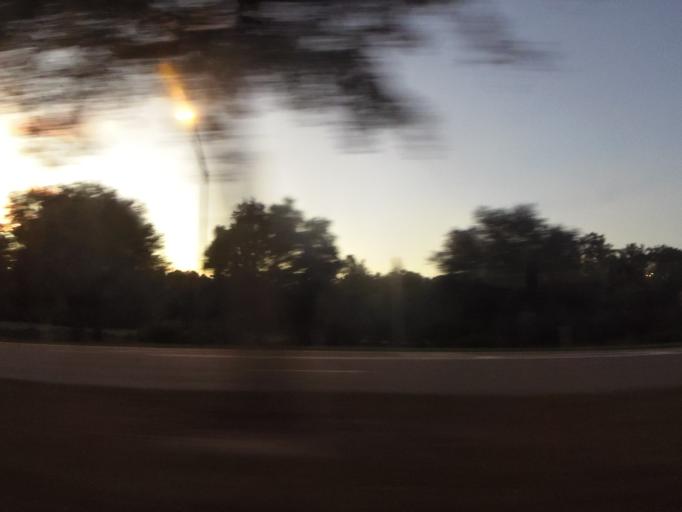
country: US
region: Florida
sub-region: Saint Johns County
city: Villano Beach
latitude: 29.9850
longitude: -81.4650
